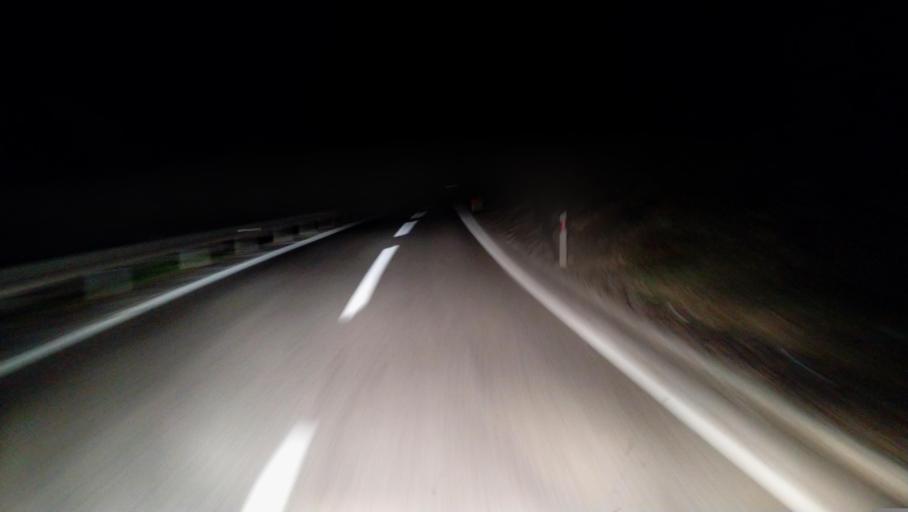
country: HR
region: Sibensko-Kniniska
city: Drnis
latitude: 43.8537
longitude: 16.1619
